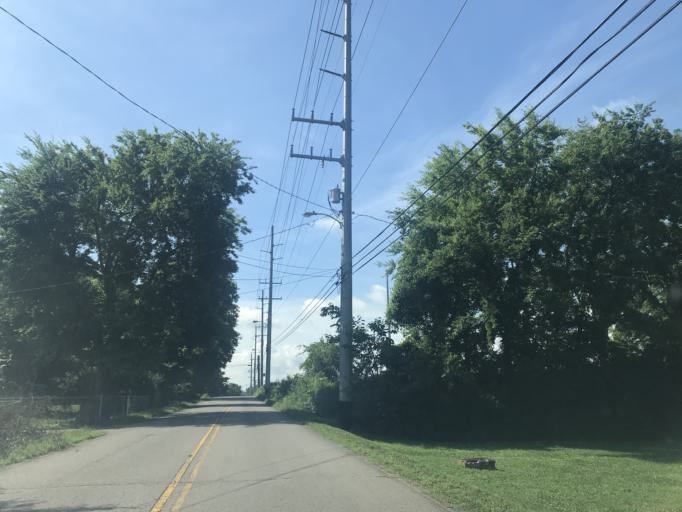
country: US
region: Tennessee
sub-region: Davidson County
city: Nashville
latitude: 36.1919
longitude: -86.8394
